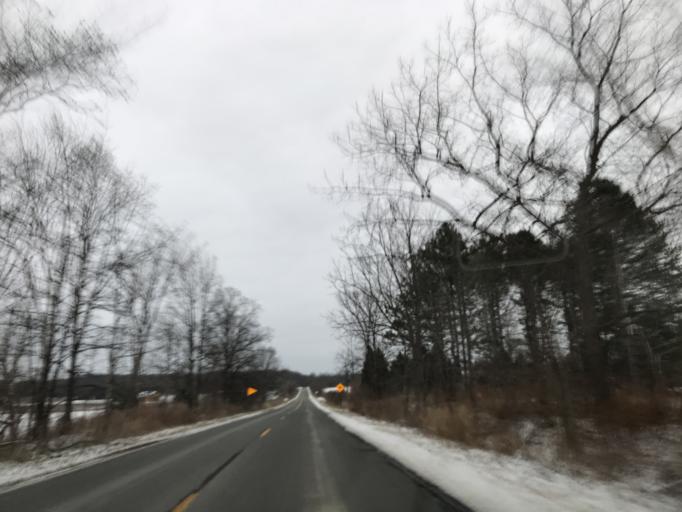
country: US
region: Michigan
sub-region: Washtenaw County
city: Ann Arbor
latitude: 42.3530
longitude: -83.6853
